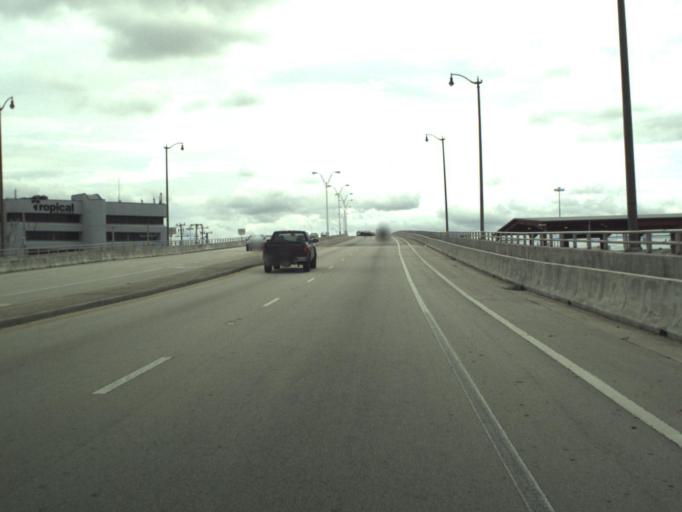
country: US
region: Florida
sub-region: Palm Beach County
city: Riviera Beach
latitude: 26.7715
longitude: -80.0552
